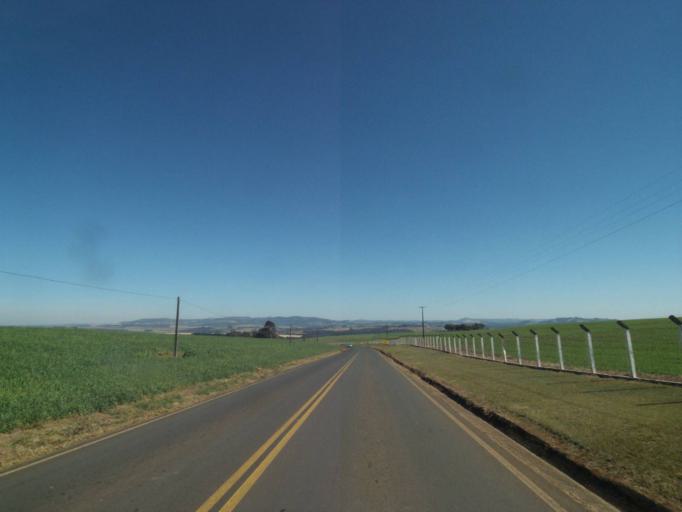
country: BR
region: Parana
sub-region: Tibagi
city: Tibagi
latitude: -24.5254
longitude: -50.3795
